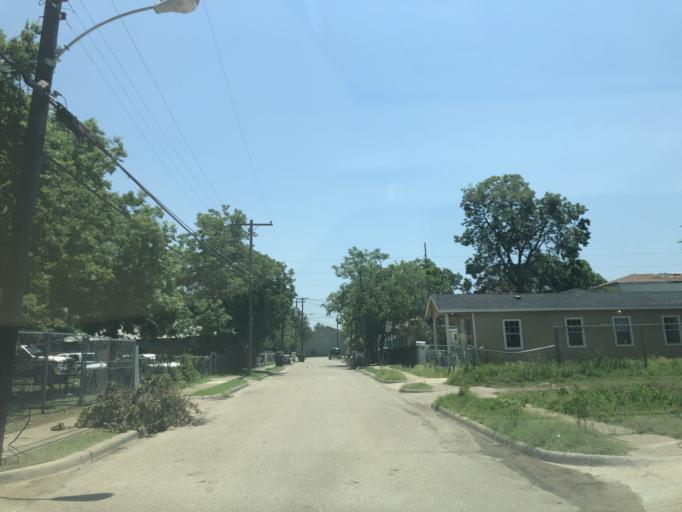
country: US
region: Texas
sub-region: Dallas County
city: Dallas
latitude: 32.7799
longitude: -96.8456
